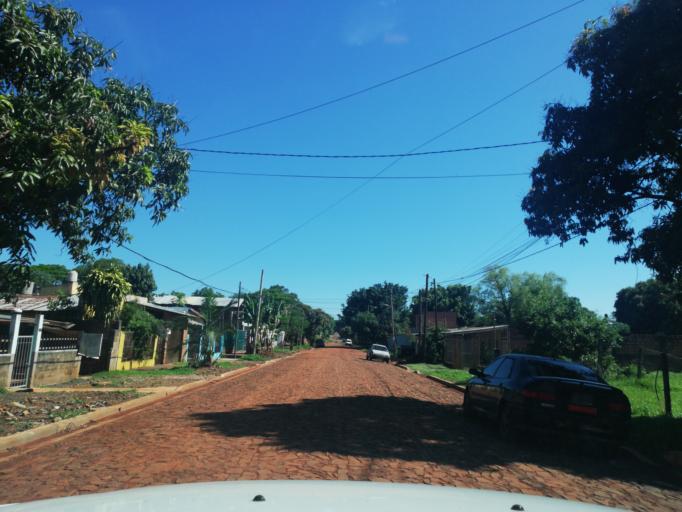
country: AR
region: Misiones
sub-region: Departamento de Capital
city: Posadas
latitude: -27.3964
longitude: -55.9225
